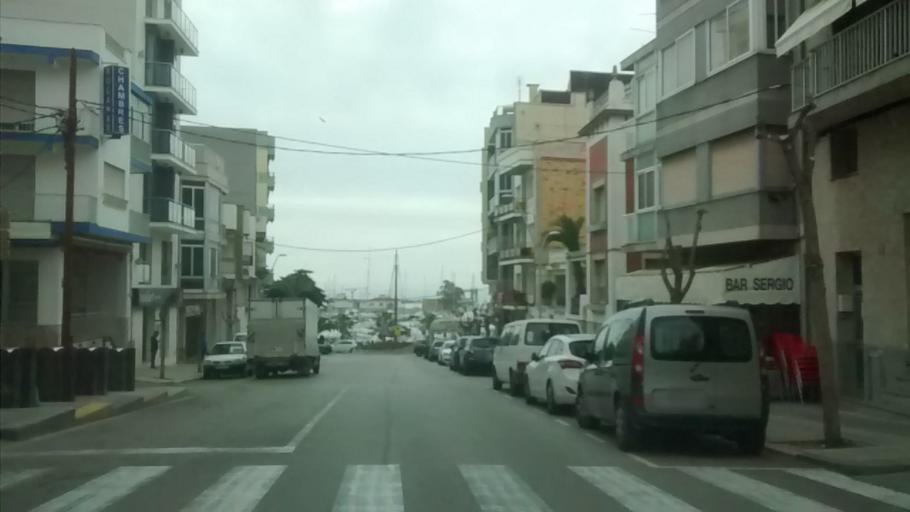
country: ES
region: Catalonia
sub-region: Provincia de Tarragona
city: Sant Carles de la Rapita
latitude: 40.6171
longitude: 0.5917
